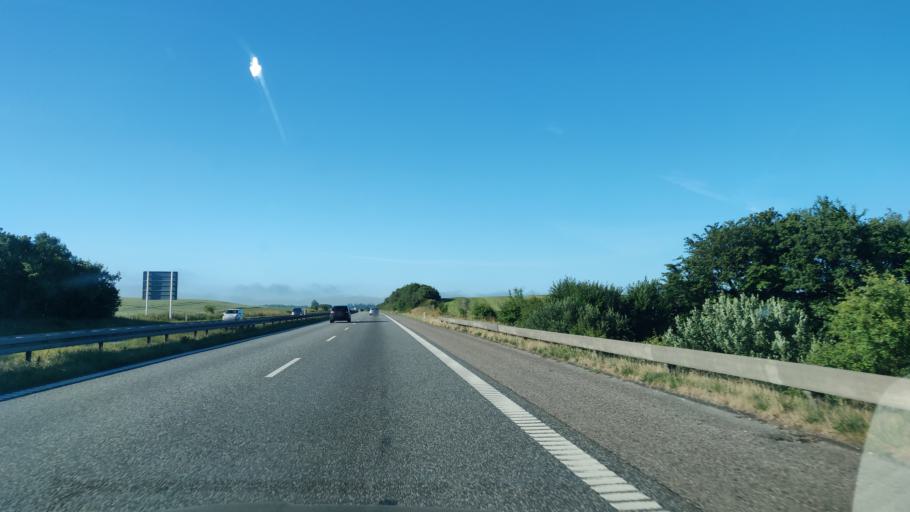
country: DK
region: North Denmark
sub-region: Mariagerfjord Kommune
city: Hobro
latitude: 56.7639
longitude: 9.6936
